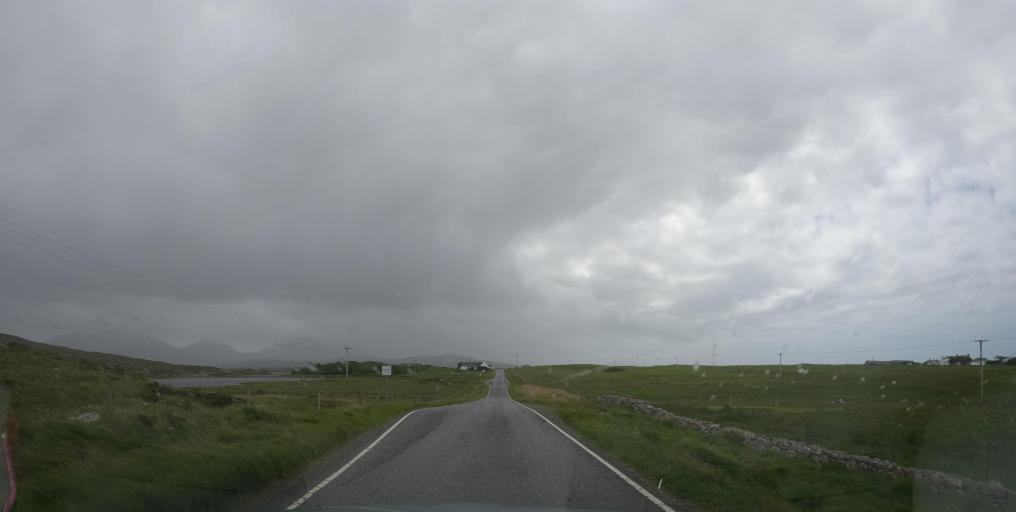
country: GB
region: Scotland
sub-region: Eilean Siar
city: Isle of South Uist
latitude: 57.3347
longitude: -7.3637
